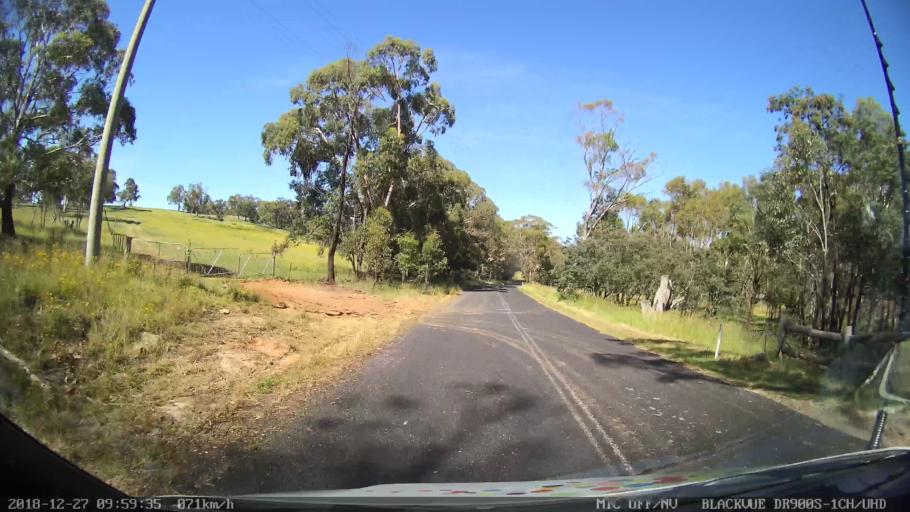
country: AU
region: New South Wales
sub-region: Lithgow
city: Portland
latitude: -33.4345
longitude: 149.9500
